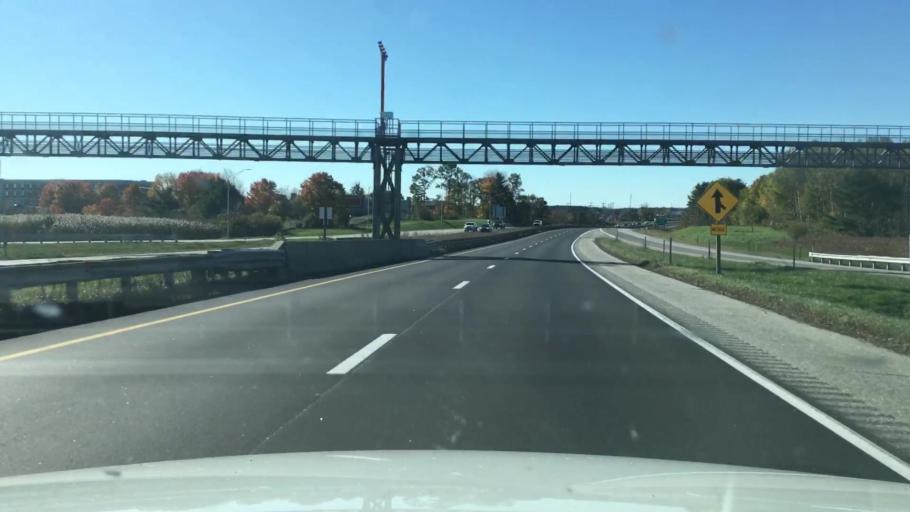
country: US
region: Maine
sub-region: Cumberland County
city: South Portland Gardens
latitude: 43.6467
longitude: -70.3319
